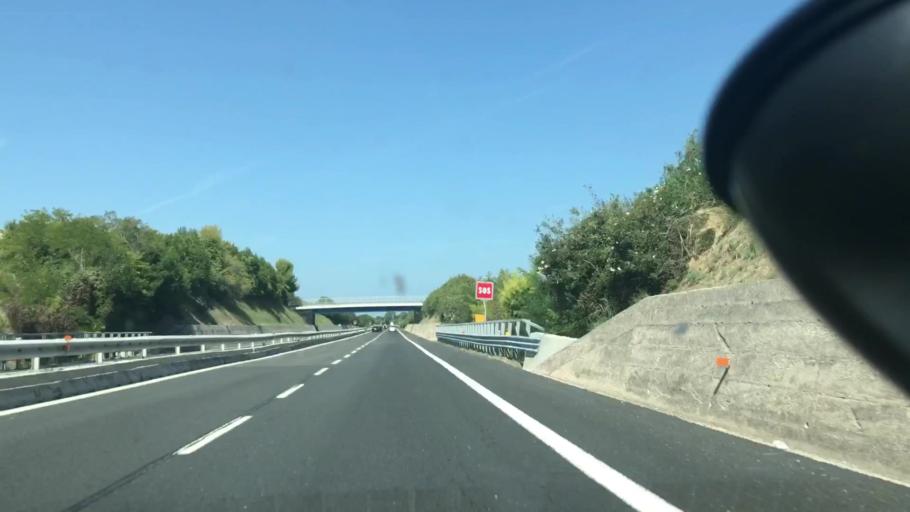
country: IT
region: Abruzzo
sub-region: Provincia di Chieti
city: Tollo
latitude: 42.3494
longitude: 14.3550
